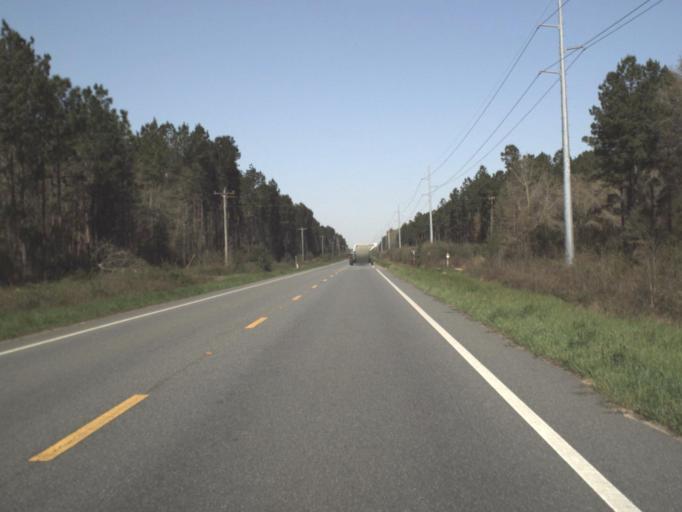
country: US
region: Alabama
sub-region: Houston County
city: Cottonwood
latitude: 30.9429
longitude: -85.3437
